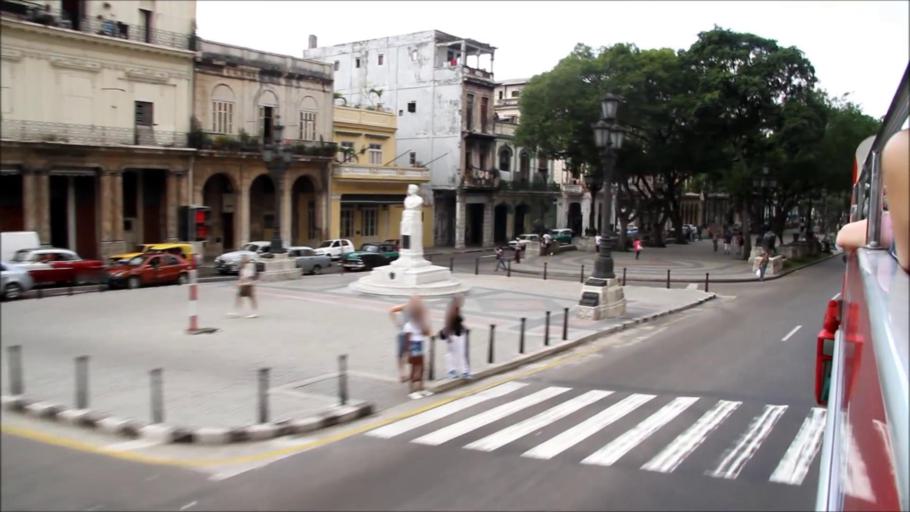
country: CU
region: La Habana
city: Centro Habana
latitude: 23.1384
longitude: -82.3593
